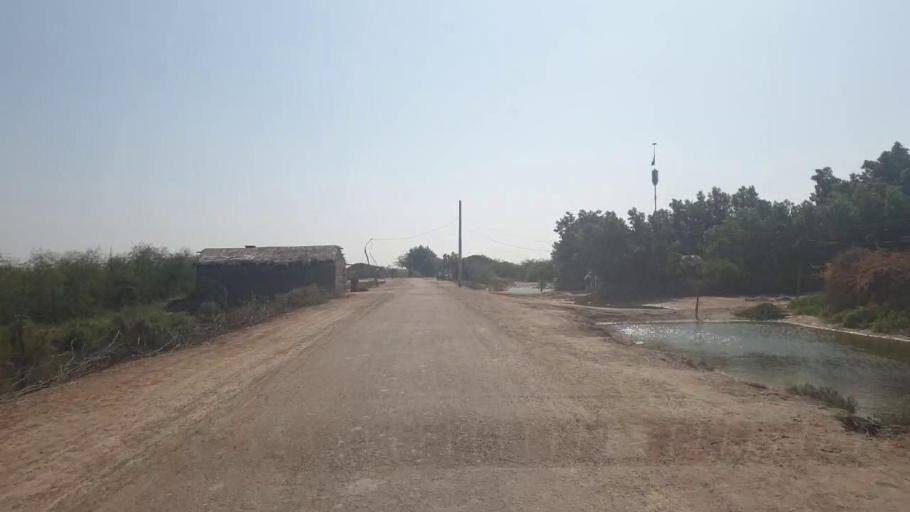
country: PK
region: Sindh
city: Badin
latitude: 24.5916
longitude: 68.8456
